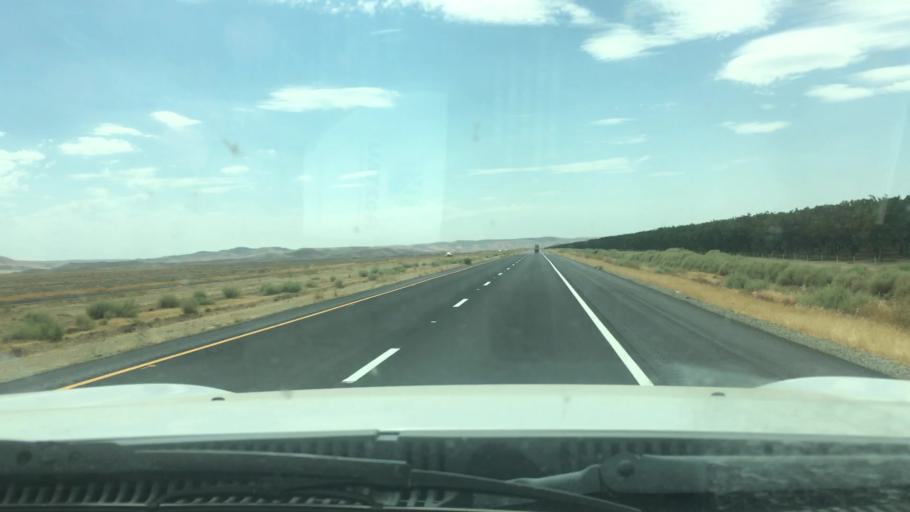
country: US
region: California
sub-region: Kern County
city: Lost Hills
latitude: 35.6148
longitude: -119.9090
